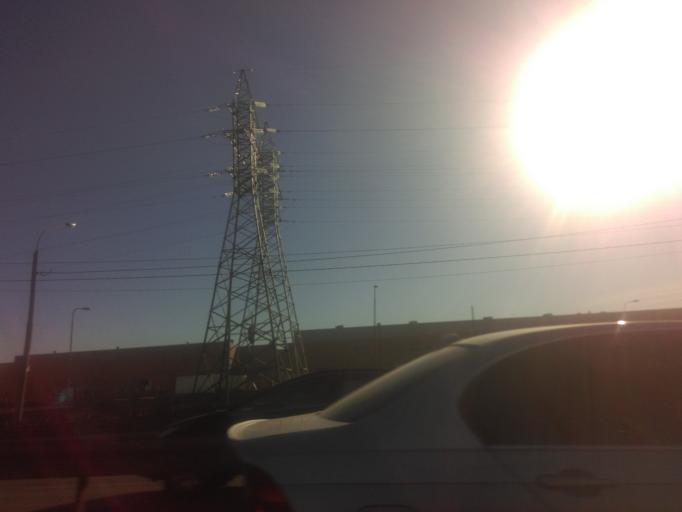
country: RU
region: Moscow
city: Tyoply Stan
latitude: 55.6065
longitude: 37.4871
